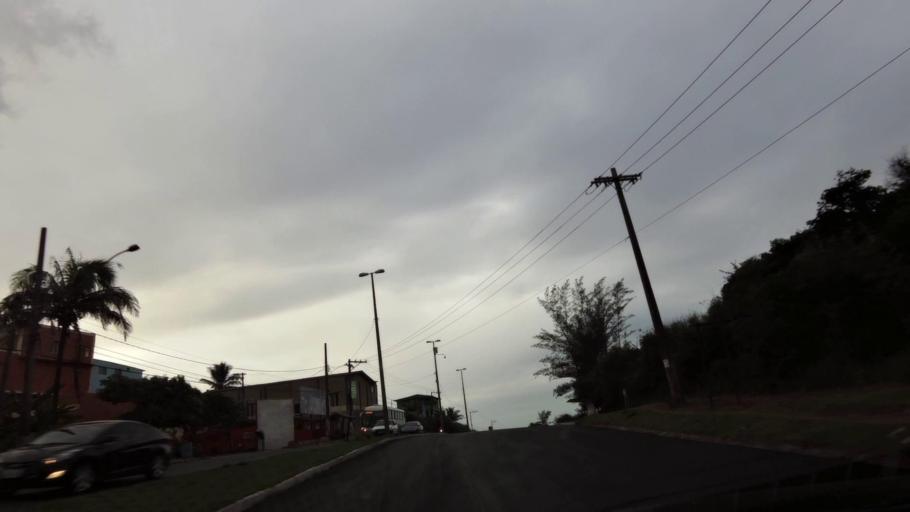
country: BR
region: Espirito Santo
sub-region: Guarapari
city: Guarapari
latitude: -20.7693
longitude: -40.5746
